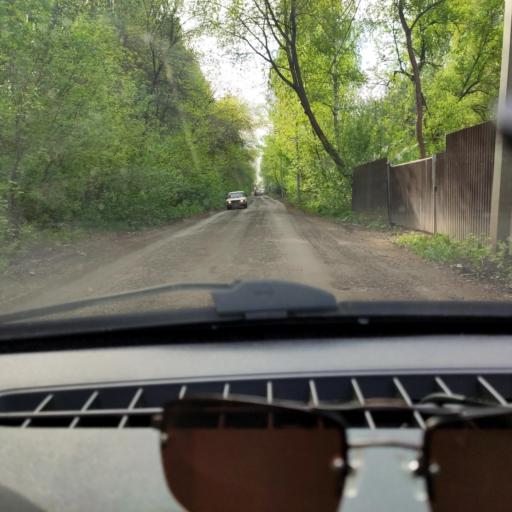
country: RU
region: Bashkortostan
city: Ufa
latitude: 54.6983
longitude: 55.9347
